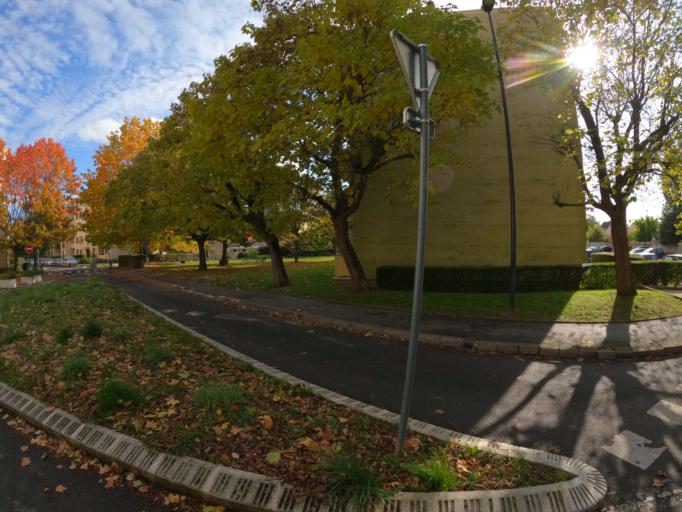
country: FR
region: Ile-de-France
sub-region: Departement de Seine-et-Marne
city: Brou-sur-Chantereine
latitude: 48.8851
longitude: 2.6276
